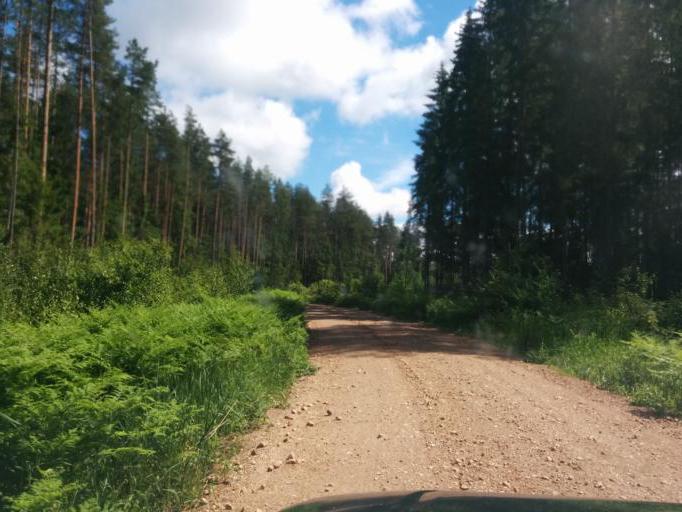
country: LV
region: Vilaka
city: Vilaka
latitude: 57.3350
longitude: 27.7045
